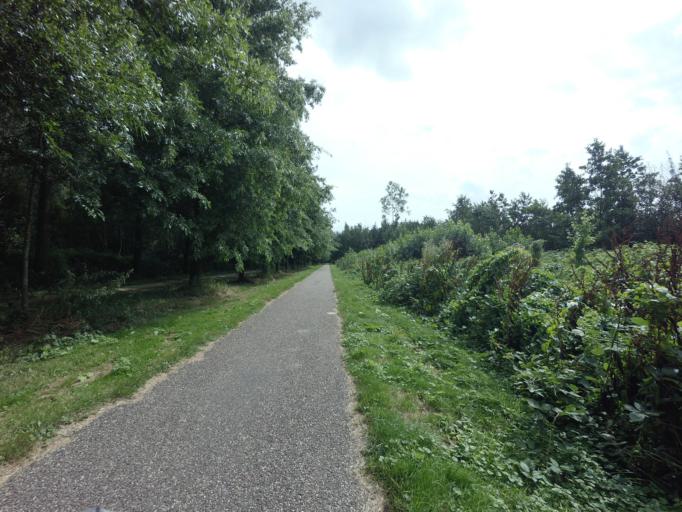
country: NL
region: North Holland
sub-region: Gemeente Amsterdam
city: Driemond
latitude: 52.3275
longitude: 5.0011
